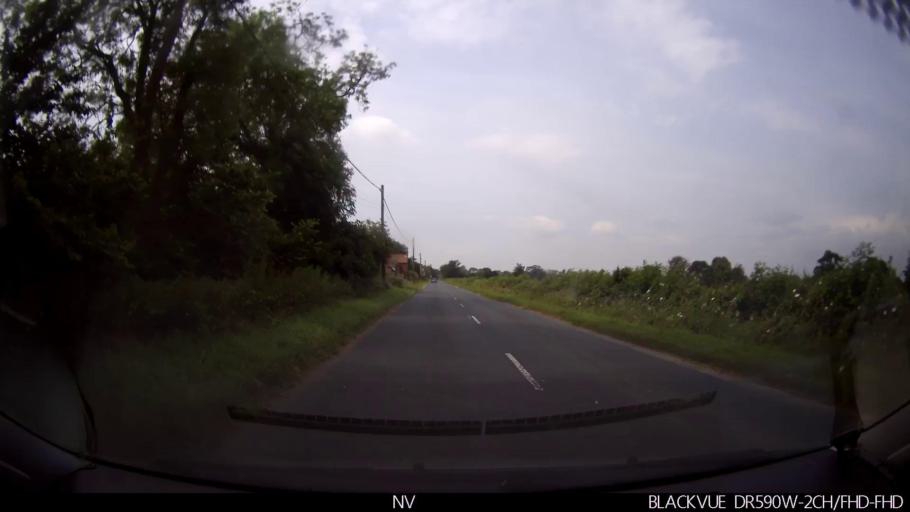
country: GB
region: England
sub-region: North Yorkshire
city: Marishes
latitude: 54.2078
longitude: -0.7887
